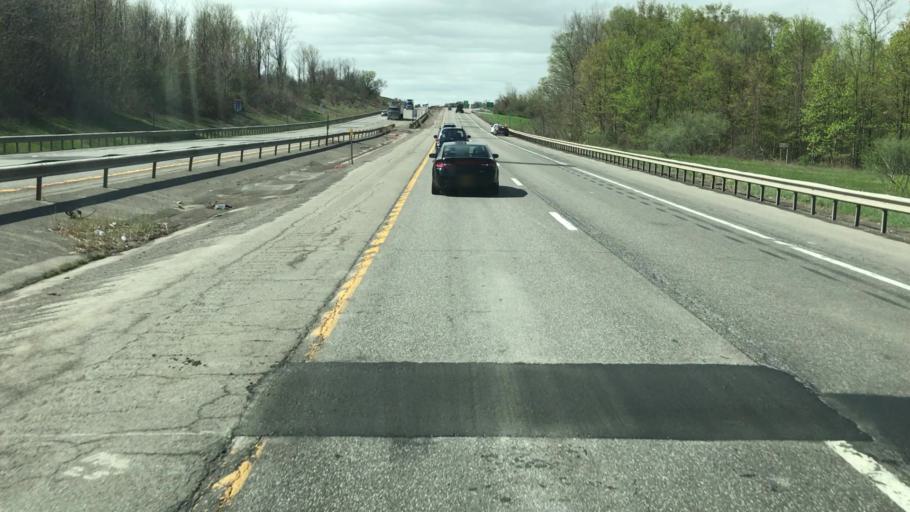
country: US
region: New York
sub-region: Onondaga County
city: Nedrow
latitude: 42.8659
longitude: -76.1145
